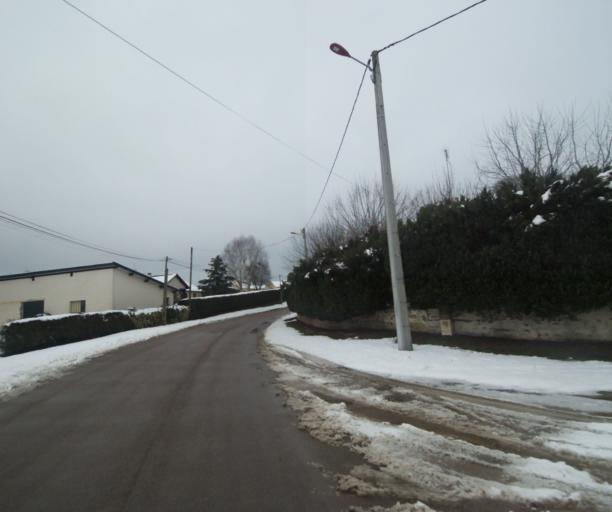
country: FR
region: Champagne-Ardenne
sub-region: Departement de la Haute-Marne
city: Laneuville-a-Remy
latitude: 48.5028
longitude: 4.8698
